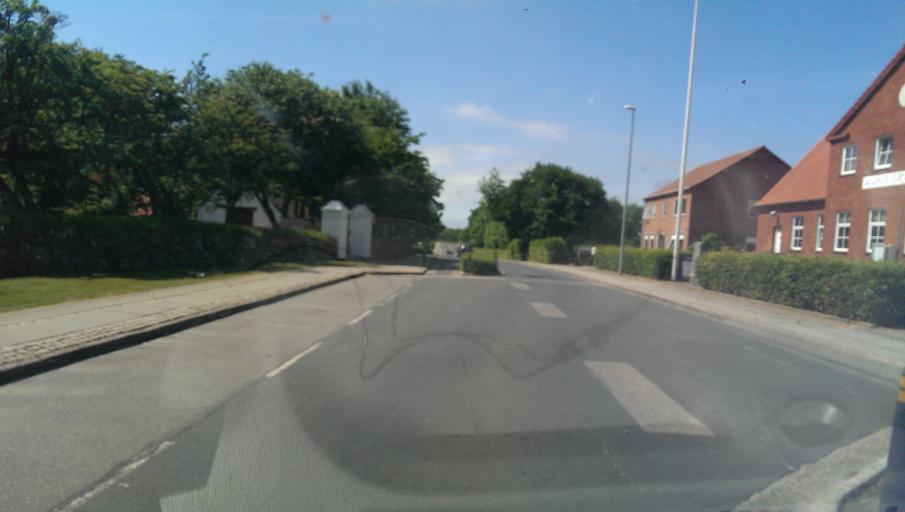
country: DK
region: South Denmark
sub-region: Esbjerg Kommune
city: Esbjerg
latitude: 55.5313
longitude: 8.4006
